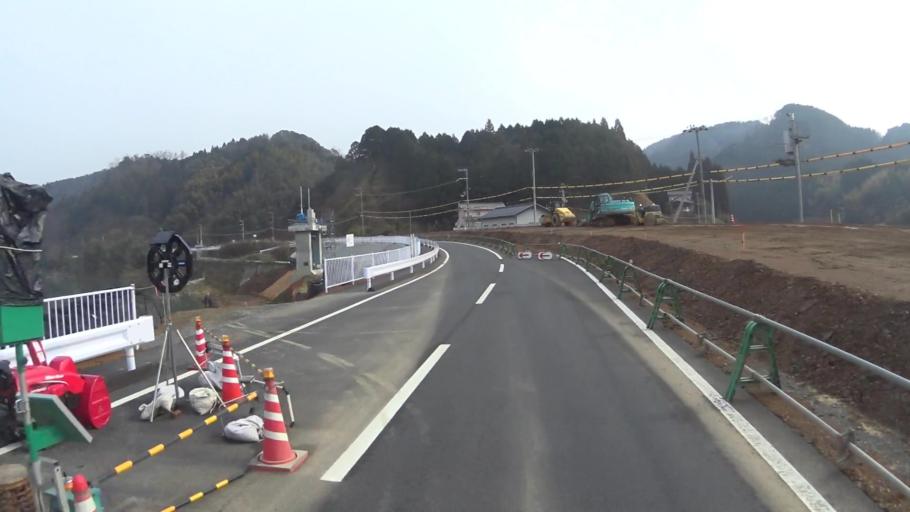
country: JP
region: Kyoto
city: Fukuchiyama
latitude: 35.3891
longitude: 135.1814
